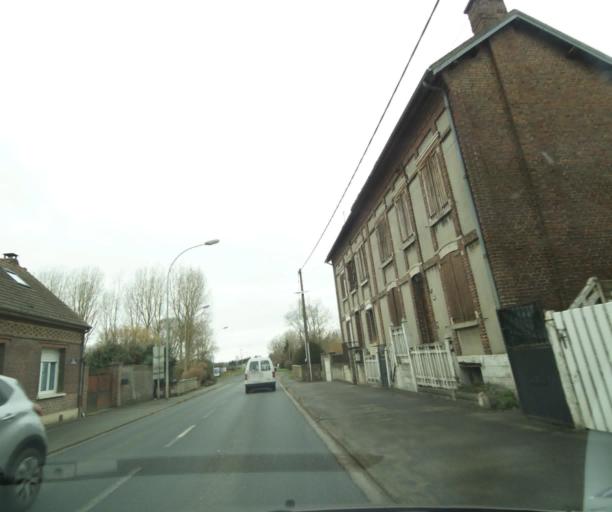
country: FR
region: Picardie
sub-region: Departement de l'Oise
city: Noyon
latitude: 49.5864
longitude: 2.9924
